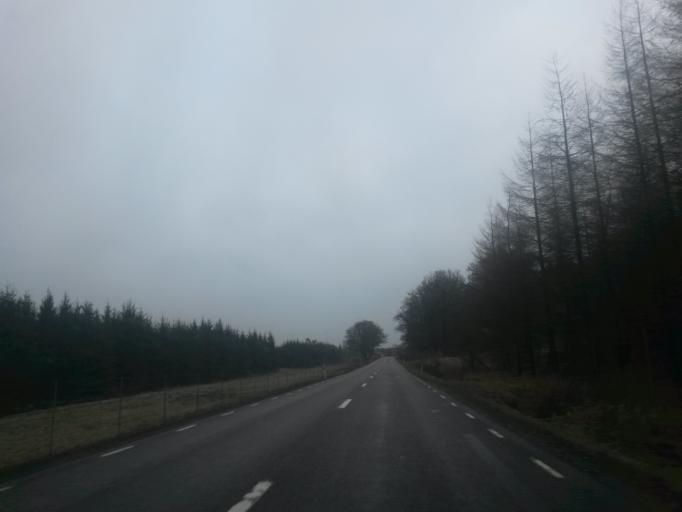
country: SE
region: Vaestra Goetaland
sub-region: Alingsas Kommun
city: Sollebrunn
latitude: 58.1530
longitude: 12.4195
